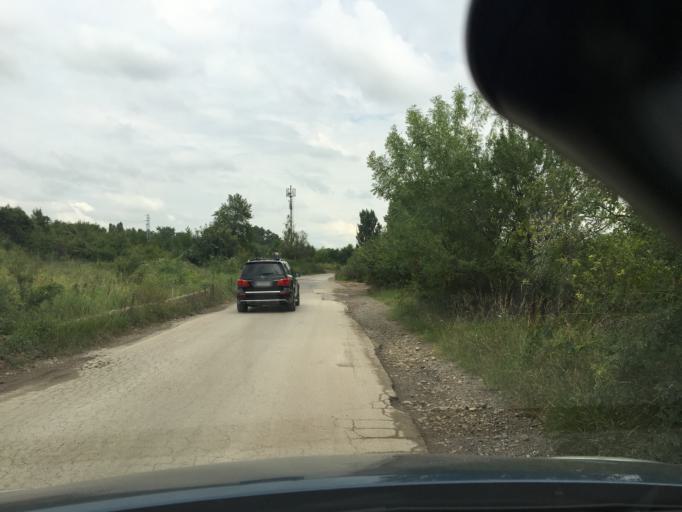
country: BG
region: Sofia-Capital
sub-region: Stolichna Obshtina
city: Sofia
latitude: 42.6159
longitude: 23.3988
